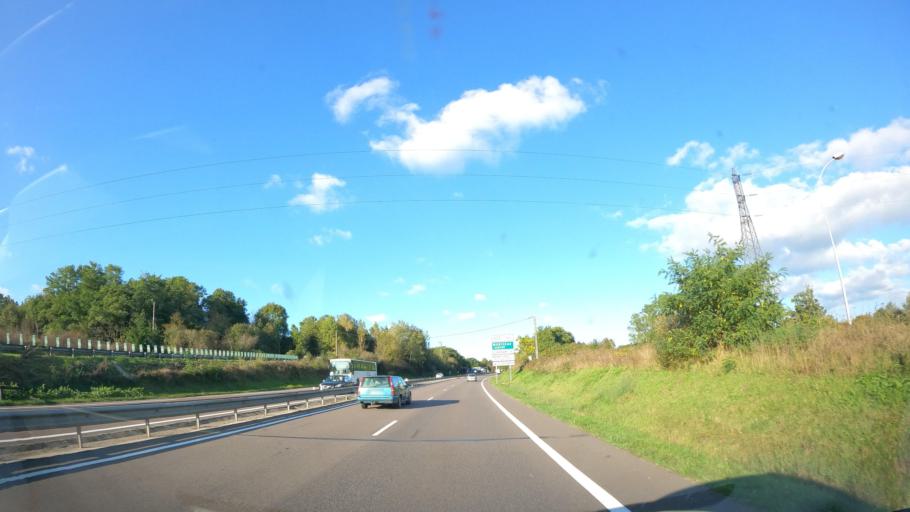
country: FR
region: Bourgogne
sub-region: Departement de Saone-et-Loire
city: Montceau-les-Mines
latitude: 46.6805
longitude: 4.3474
